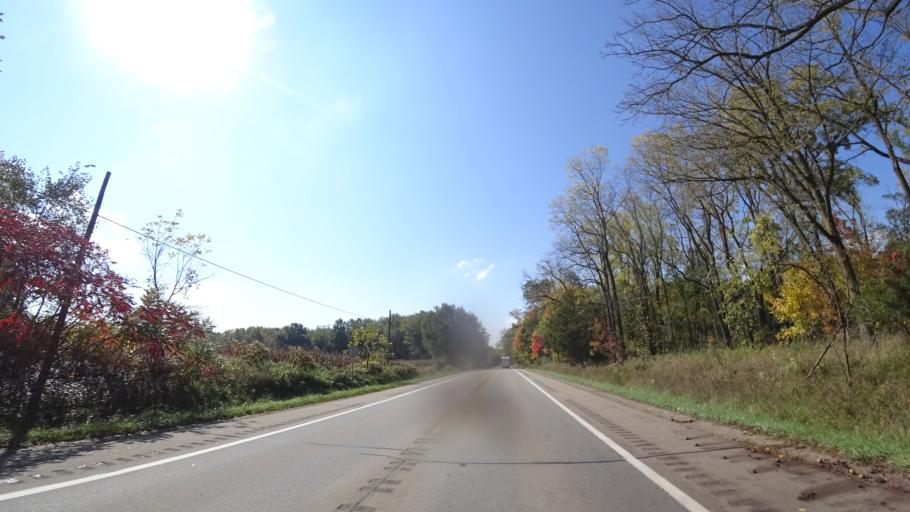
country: US
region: Michigan
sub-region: Jackson County
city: Spring Arbor
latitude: 42.1959
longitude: -84.5948
